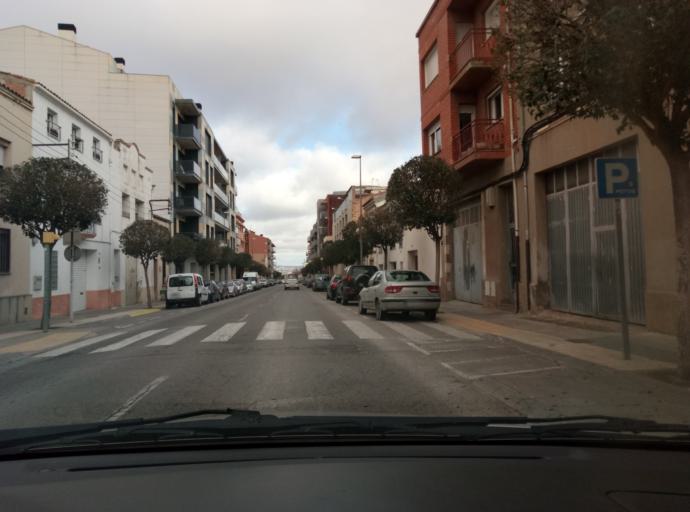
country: ES
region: Catalonia
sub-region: Provincia de Lleida
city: Tarrega
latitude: 41.6537
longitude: 1.1380
